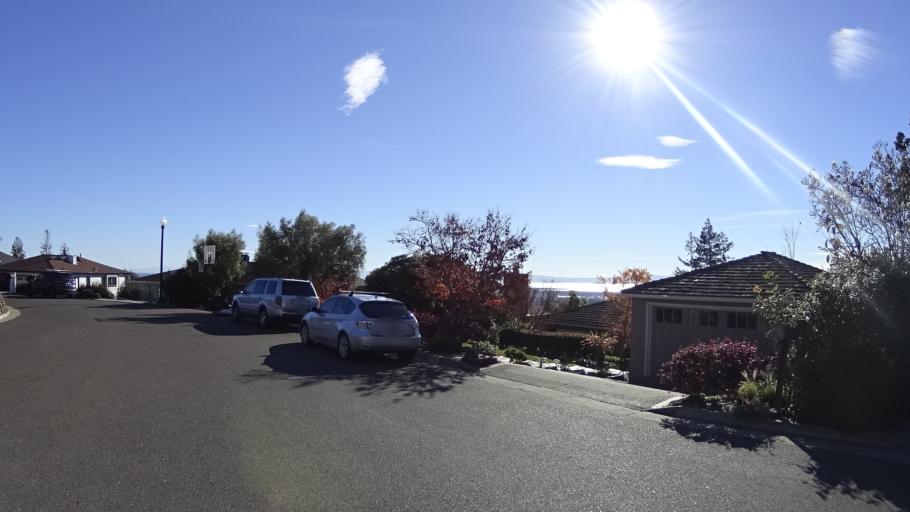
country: US
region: California
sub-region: Alameda County
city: Piedmont
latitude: 37.8259
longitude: -122.2237
